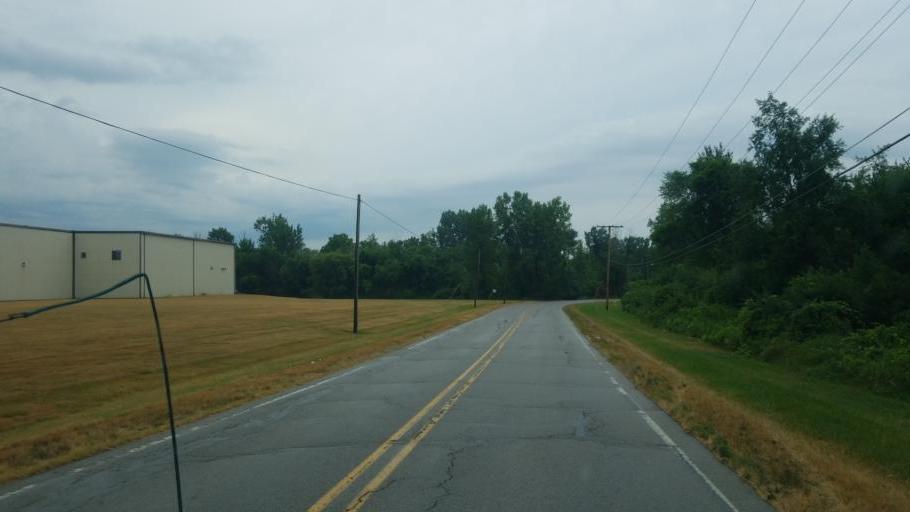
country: US
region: Indiana
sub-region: Steuben County
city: Hamilton
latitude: 41.5354
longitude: -84.9296
